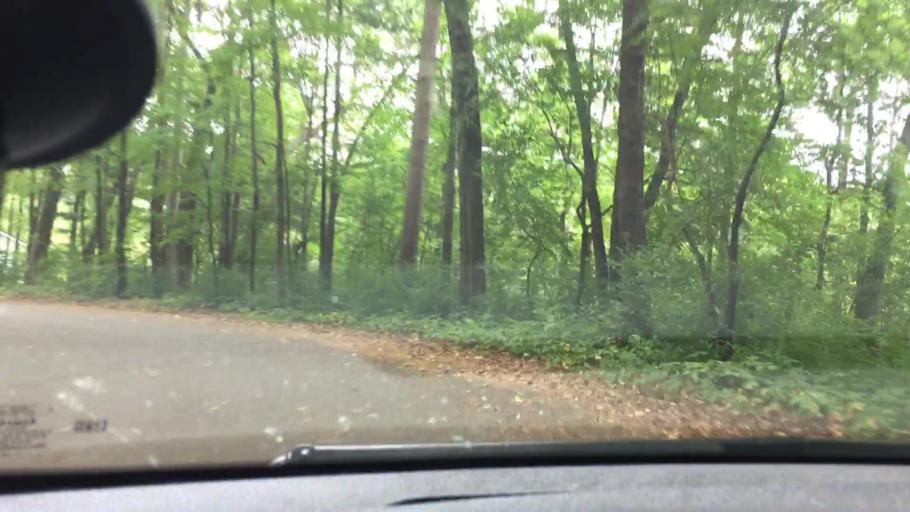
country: US
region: Wisconsin
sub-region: Chippewa County
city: Chippewa Falls
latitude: 44.9657
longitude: -91.4021
